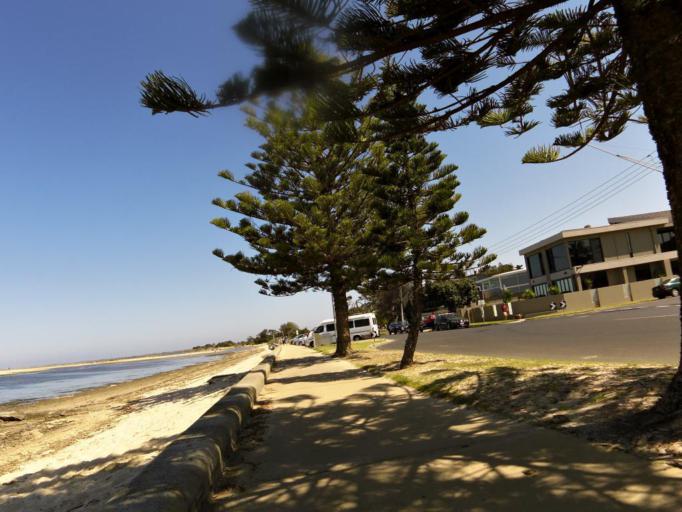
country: AU
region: Victoria
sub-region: Hobsons Bay
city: Altona
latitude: -37.8747
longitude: 144.8151
